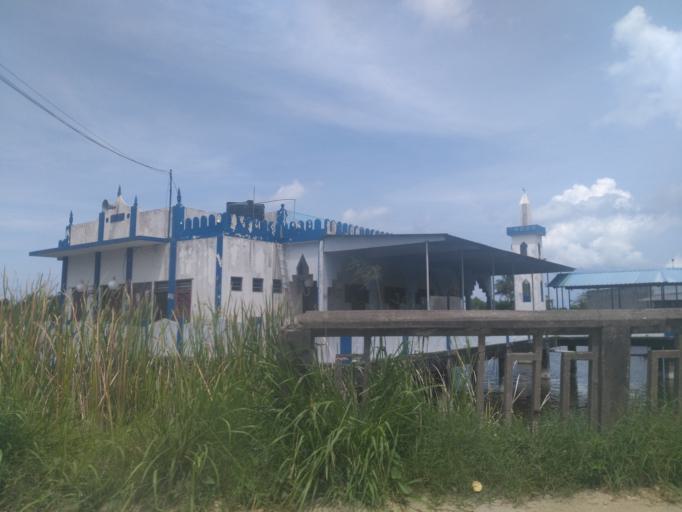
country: TZ
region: Zanzibar Urban/West
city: Zanzibar
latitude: -6.1587
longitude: 39.2013
